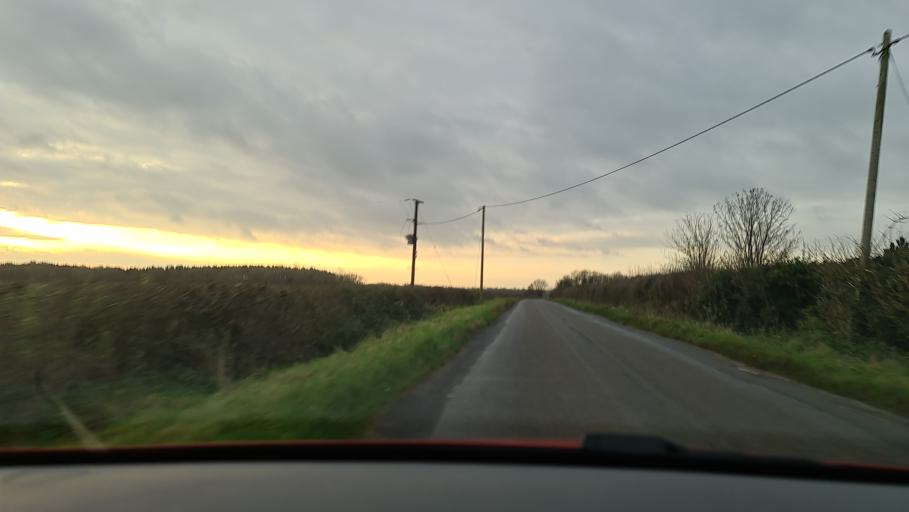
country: GB
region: England
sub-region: Oxfordshire
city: Somerton
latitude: 51.9081
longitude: -1.2751
